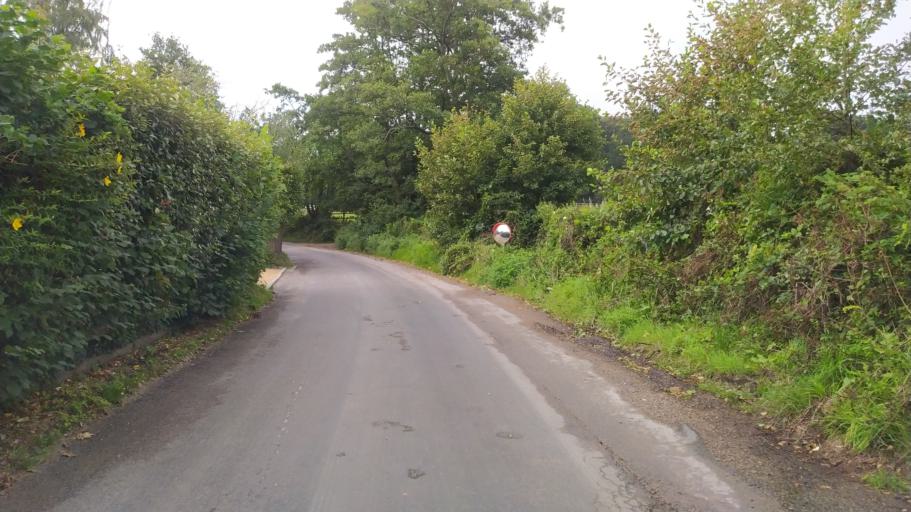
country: GB
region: England
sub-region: Dorset
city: Lytchett Matravers
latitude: 50.7779
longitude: -2.0360
